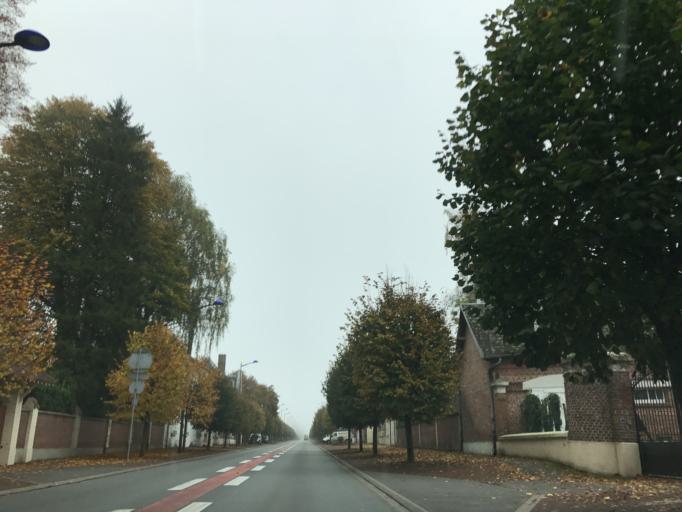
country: FR
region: Nord-Pas-de-Calais
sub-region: Departement du Pas-de-Calais
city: Bapaume
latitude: 50.0975
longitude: 2.8578
